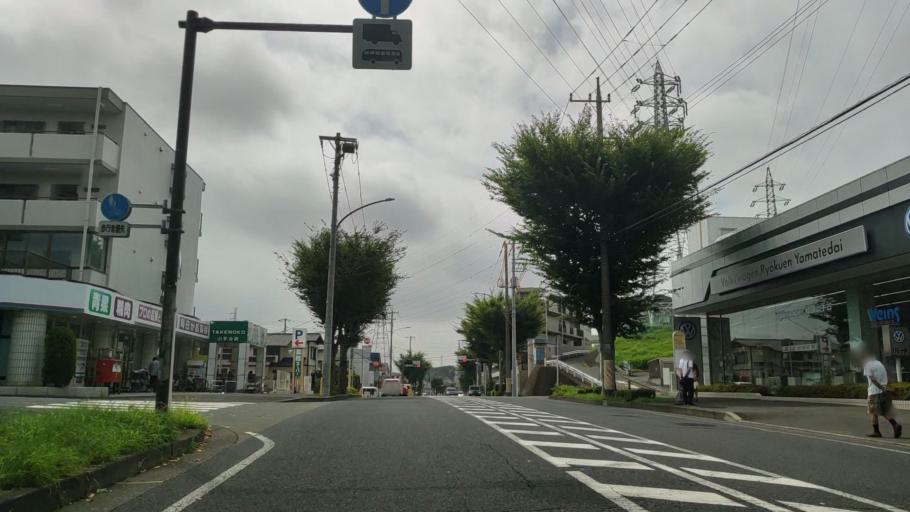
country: JP
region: Kanagawa
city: Fujisawa
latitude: 35.4166
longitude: 139.5228
